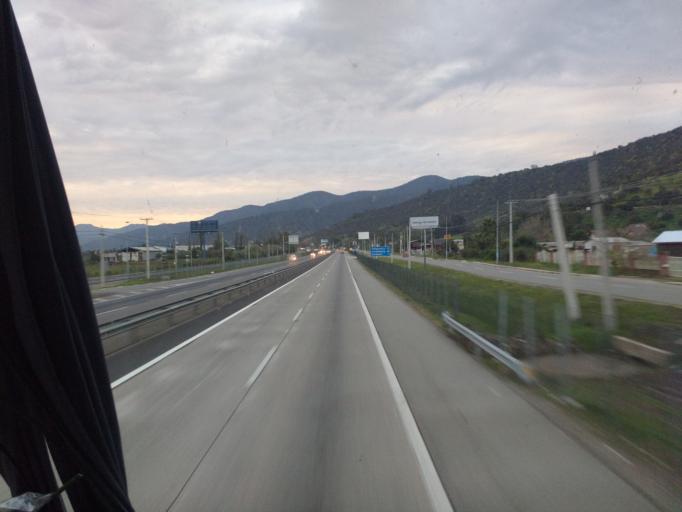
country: CL
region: Santiago Metropolitan
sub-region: Provincia de Chacabuco
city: Lampa
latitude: -33.4170
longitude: -71.0501
